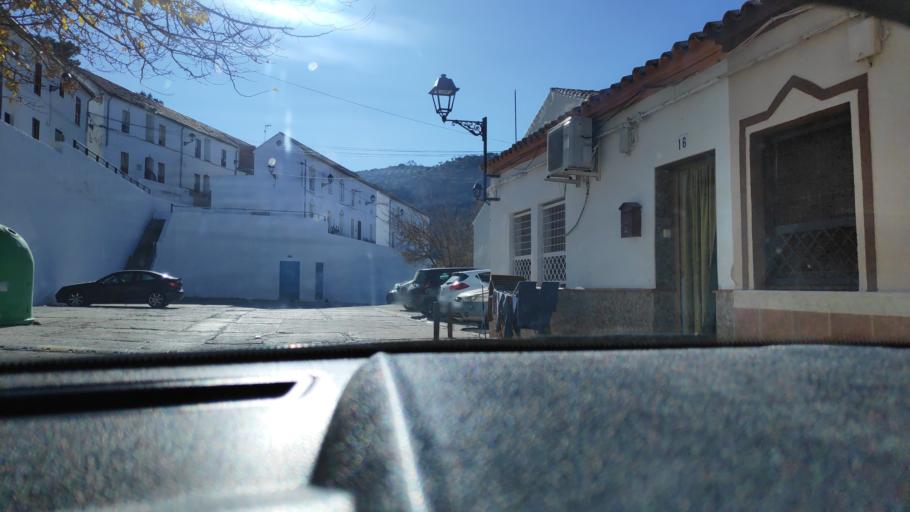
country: ES
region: Andalusia
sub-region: Province of Cordoba
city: Baena
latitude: 37.6123
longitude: -4.3333
